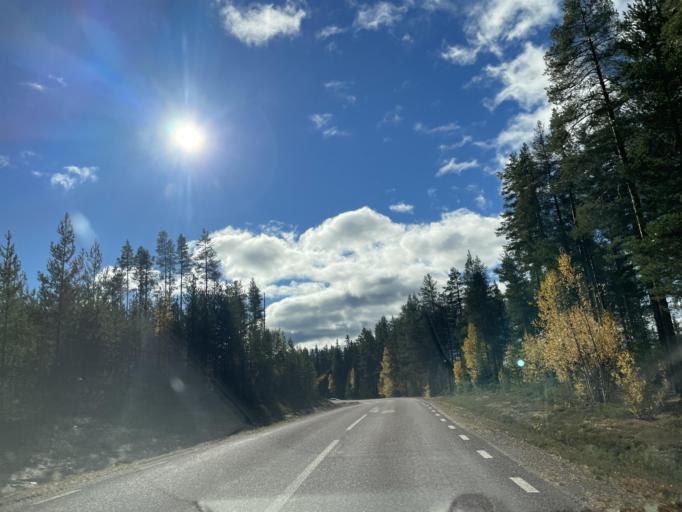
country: NO
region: Hedmark
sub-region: Trysil
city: Innbygda
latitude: 61.4626
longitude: 13.0914
